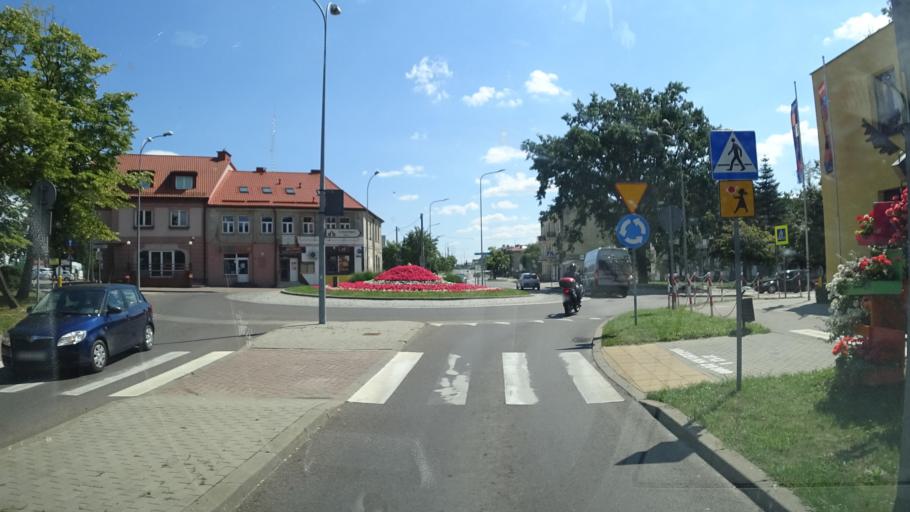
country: PL
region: Podlasie
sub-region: Lomza
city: Lomza
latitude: 53.1747
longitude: 22.0789
